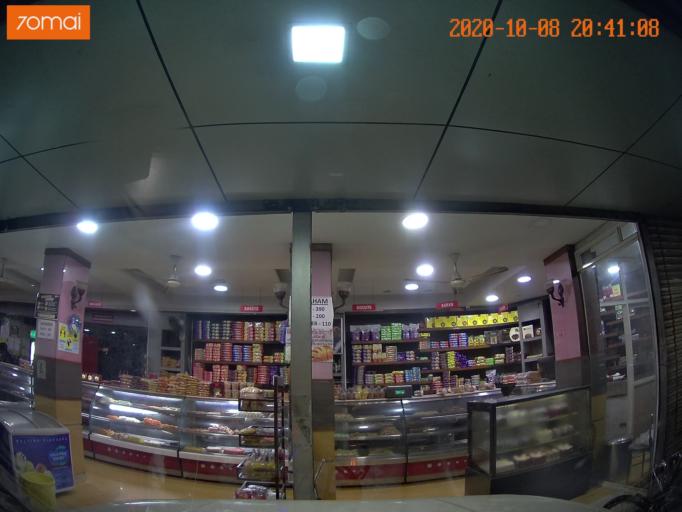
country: IN
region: Kerala
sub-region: Kozhikode
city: Kozhikode
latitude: 11.2365
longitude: 75.8044
